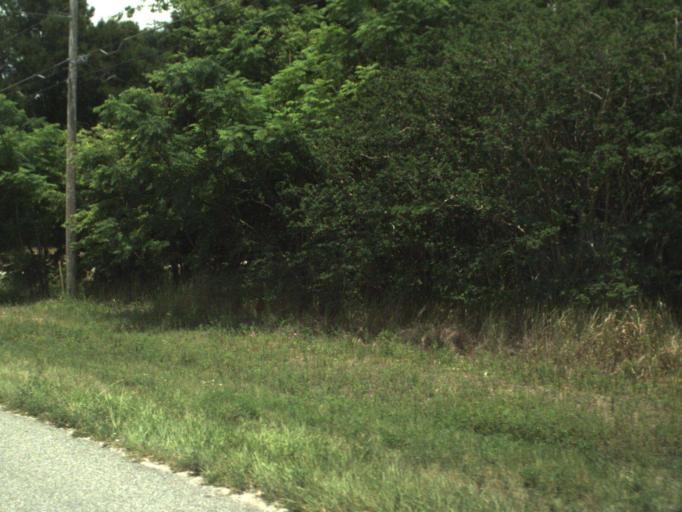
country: US
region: Florida
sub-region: Marion County
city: Silver Springs Shores
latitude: 29.1280
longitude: -82.0536
